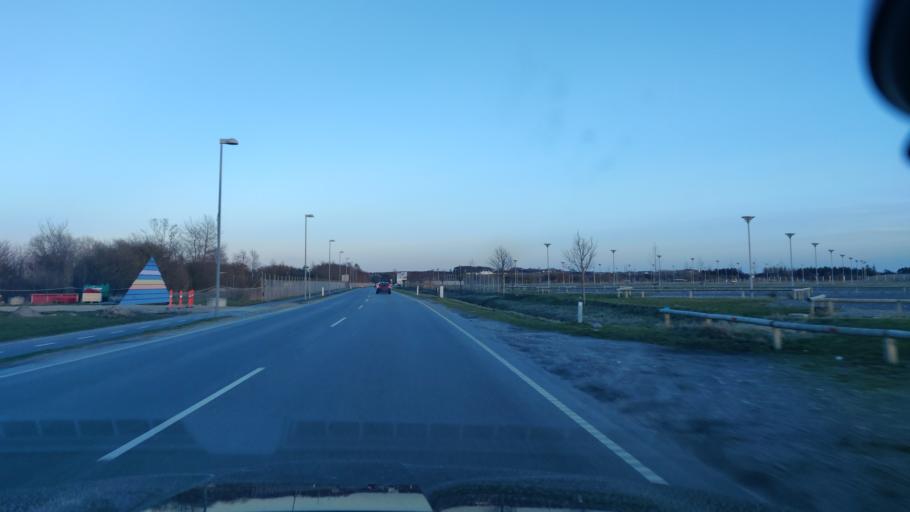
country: DK
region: North Denmark
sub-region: Alborg Kommune
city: Vadum
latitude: 57.0856
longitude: 9.8797
